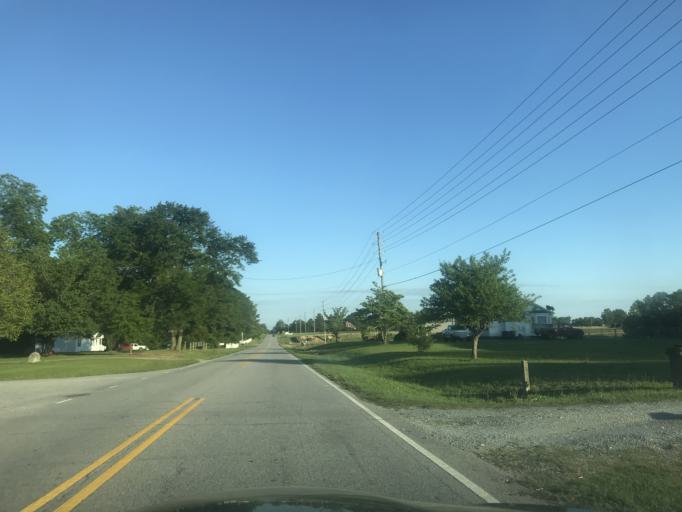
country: US
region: North Carolina
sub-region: Johnston County
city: Archer Lodge
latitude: 35.6797
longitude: -78.3619
